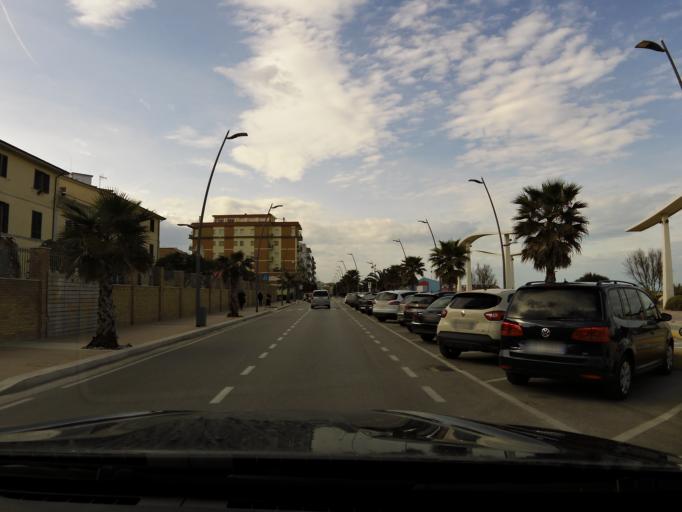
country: IT
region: The Marches
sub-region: Provincia di Macerata
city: Portocivitanova
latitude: 43.3133
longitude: 13.7261
